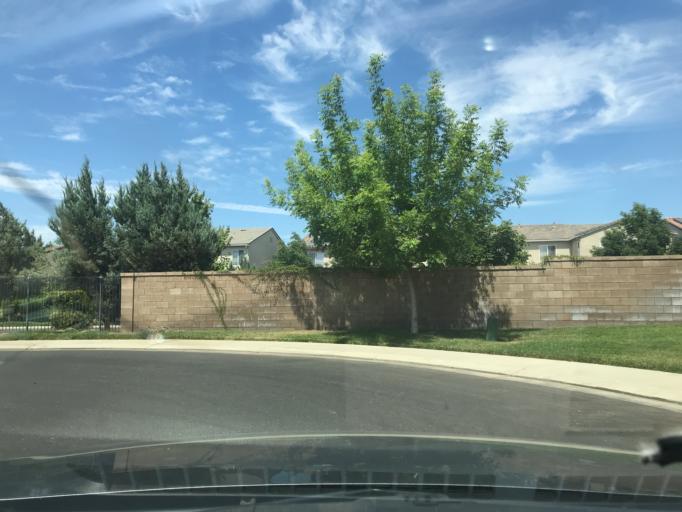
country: US
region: California
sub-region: Merced County
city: Merced
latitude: 37.3398
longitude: -120.4949
